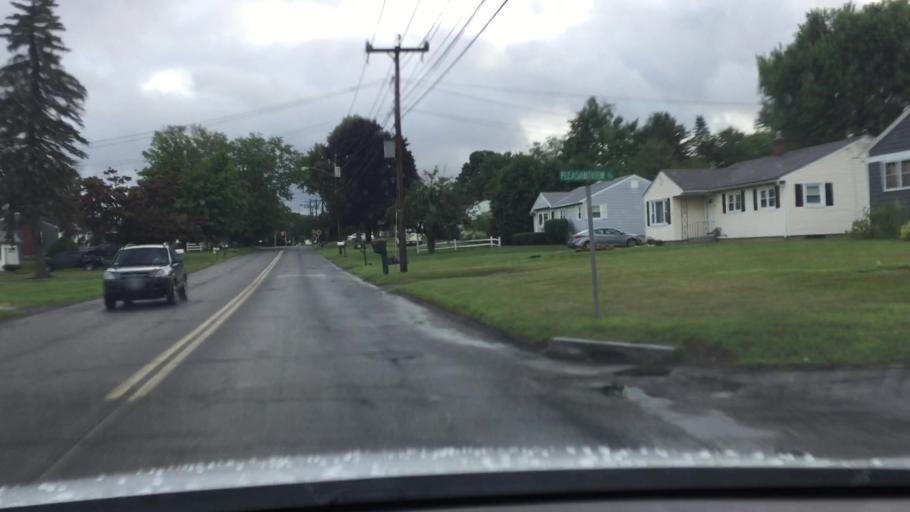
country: US
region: Massachusetts
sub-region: Berkshire County
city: Dalton
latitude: 42.4496
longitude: -73.1916
